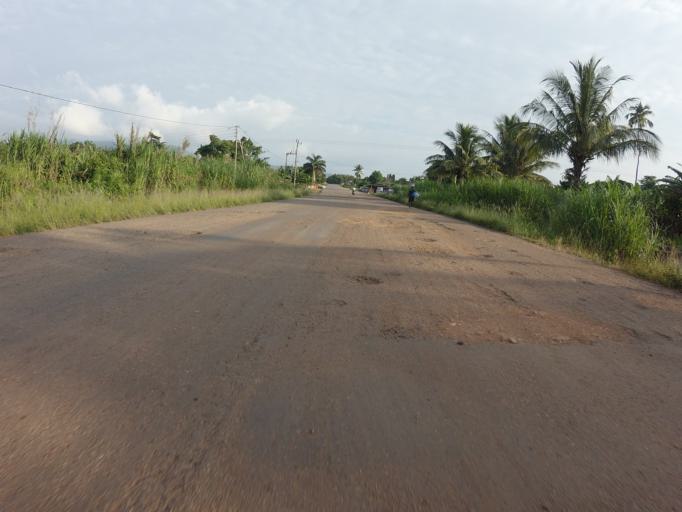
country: GH
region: Volta
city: Kpandu
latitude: 6.9566
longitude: 0.4584
